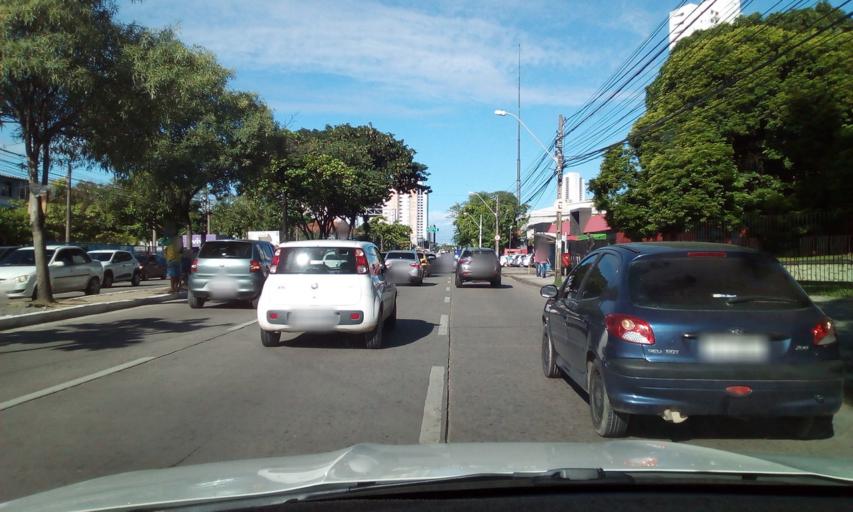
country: BR
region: Pernambuco
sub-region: Recife
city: Recife
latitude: -8.0613
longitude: -34.9040
